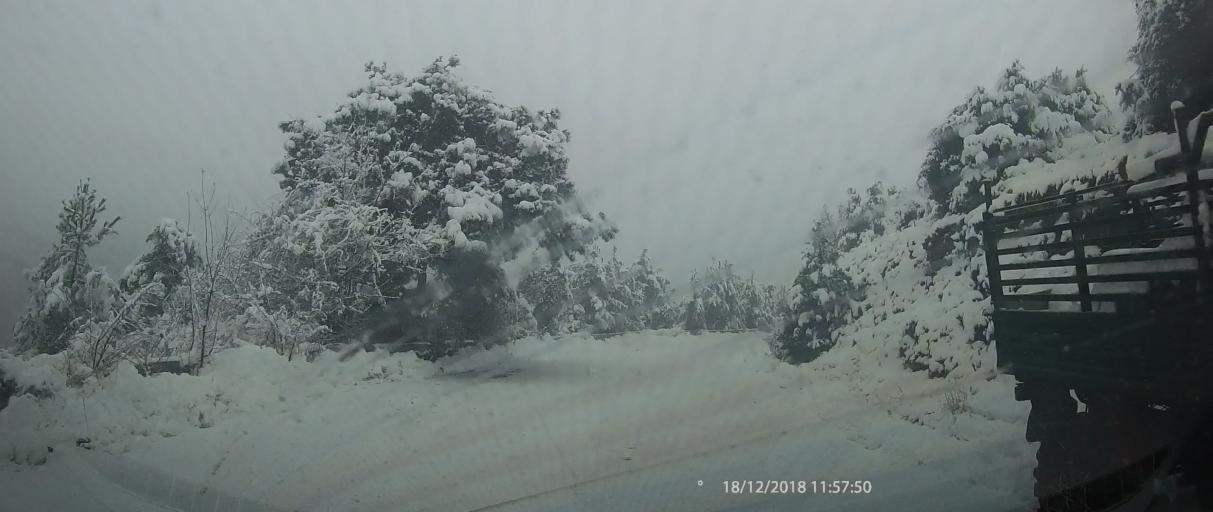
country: GR
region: Central Macedonia
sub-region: Nomos Pierias
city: Litochoro
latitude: 40.1116
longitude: 22.4683
